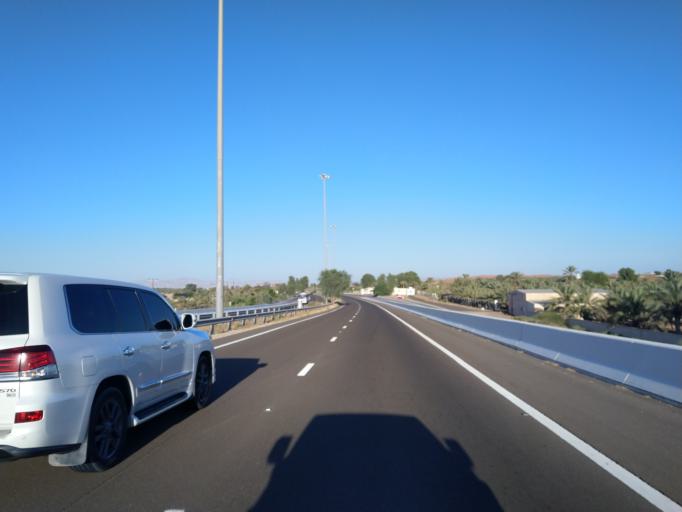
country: OM
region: Al Buraimi
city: Al Buraymi
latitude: 24.5506
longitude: 55.6805
